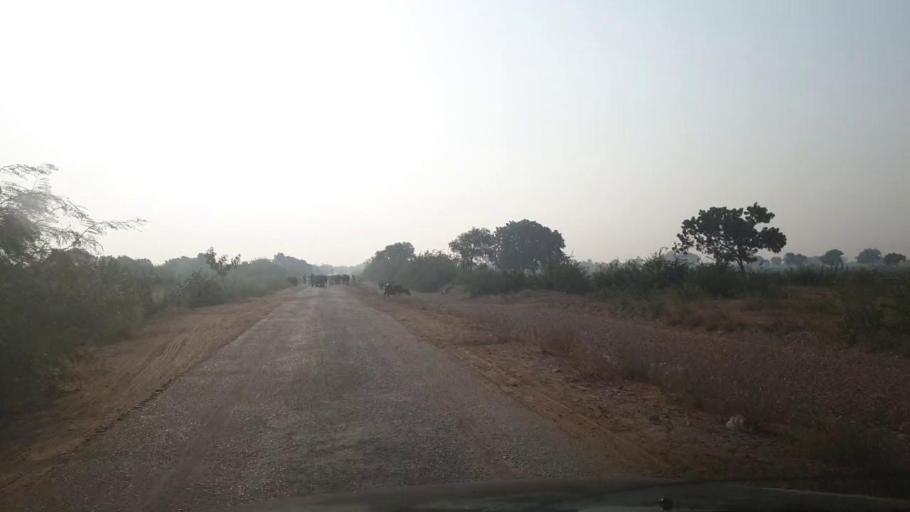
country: PK
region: Sindh
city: Kotri
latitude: 25.3189
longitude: 68.2339
